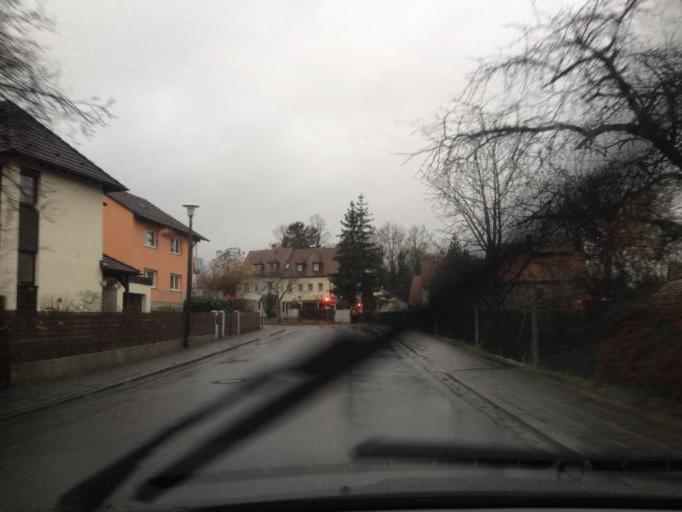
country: DE
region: Bavaria
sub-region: Regierungsbezirk Mittelfranken
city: Schwaig
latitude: 49.4741
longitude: 11.1993
